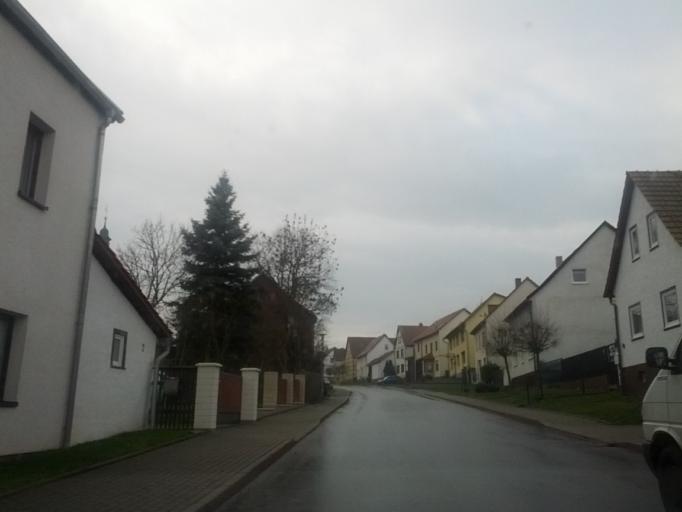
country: DE
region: Thuringia
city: Friedrichswerth
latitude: 50.9741
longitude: 10.5392
